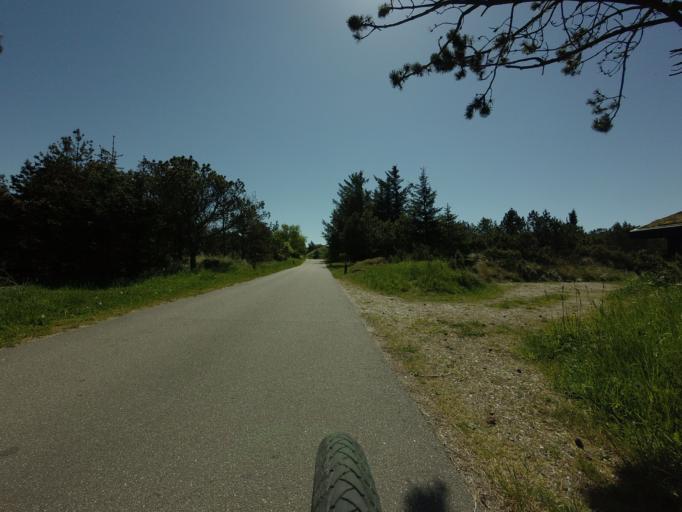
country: DK
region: North Denmark
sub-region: Jammerbugt Kommune
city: Pandrup
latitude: 57.2293
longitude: 9.5620
